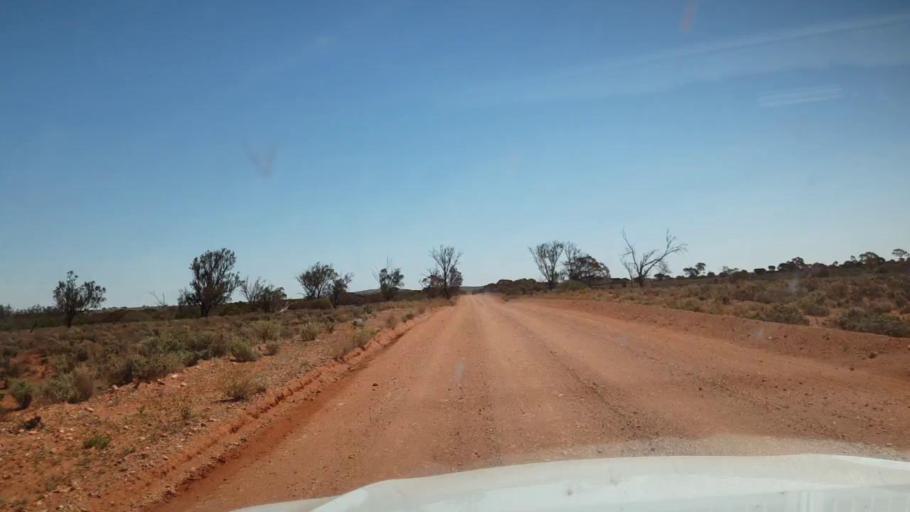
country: AU
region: South Australia
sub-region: Whyalla
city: Whyalla
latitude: -32.6843
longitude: 137.1026
